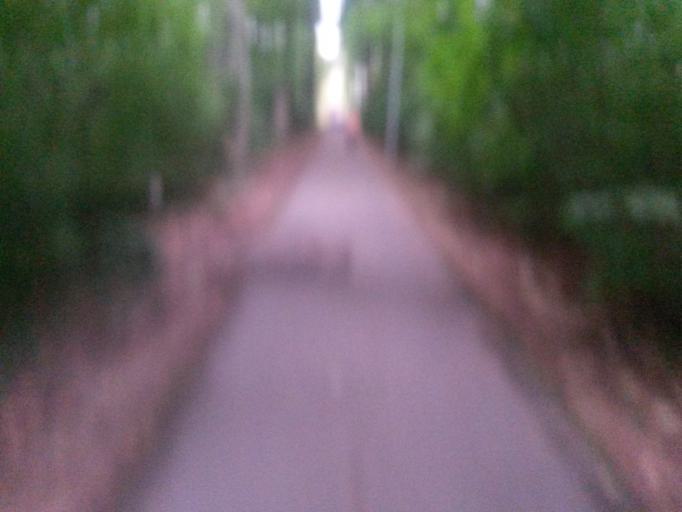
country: DE
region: Bavaria
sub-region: Upper Palatinate
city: Amberg
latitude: 49.4513
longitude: 11.8734
